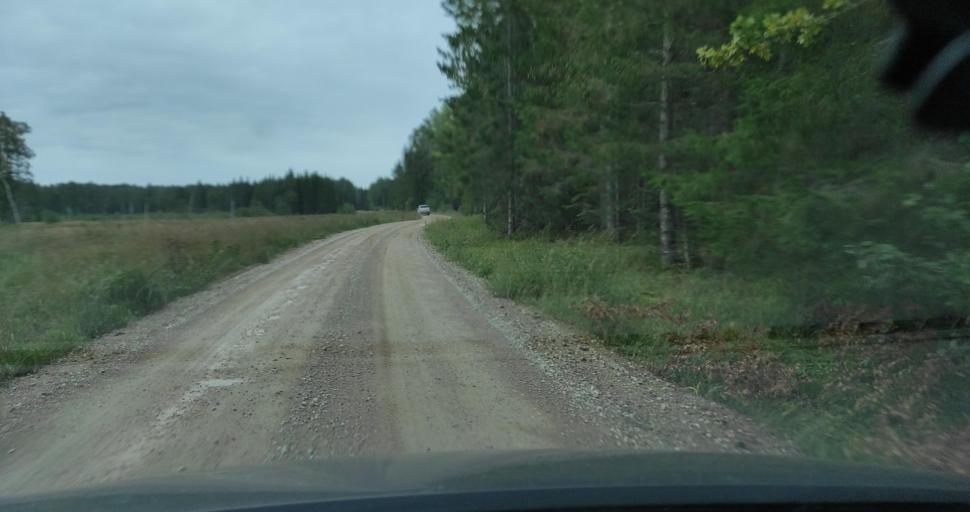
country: LV
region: Talsu Rajons
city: Stende
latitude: 57.0245
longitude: 22.3485
